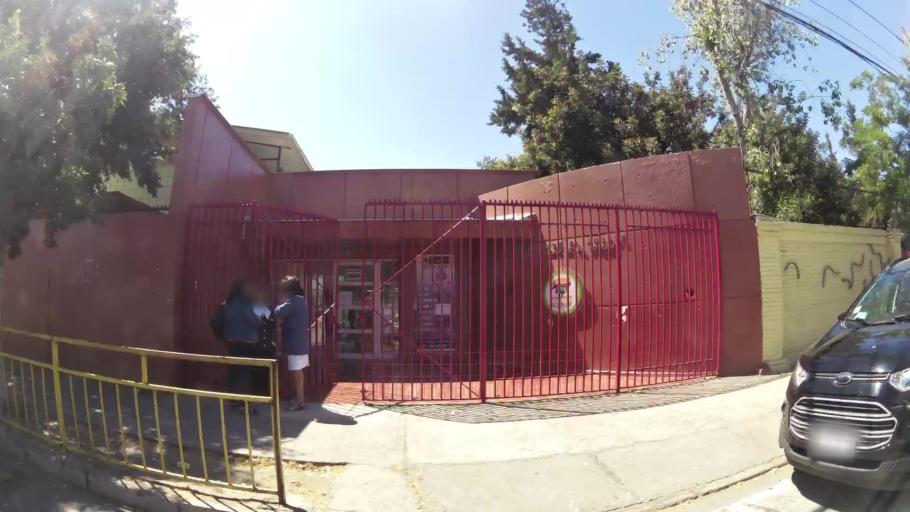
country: CL
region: Santiago Metropolitan
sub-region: Provincia de Maipo
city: San Bernardo
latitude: -33.5620
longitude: -70.6753
